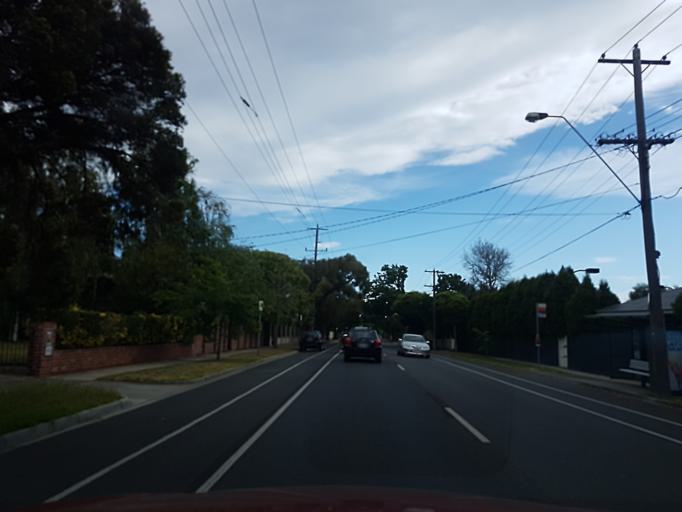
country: AU
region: Victoria
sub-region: Glen Eira
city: Caulfield
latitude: -37.8868
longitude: 145.0149
